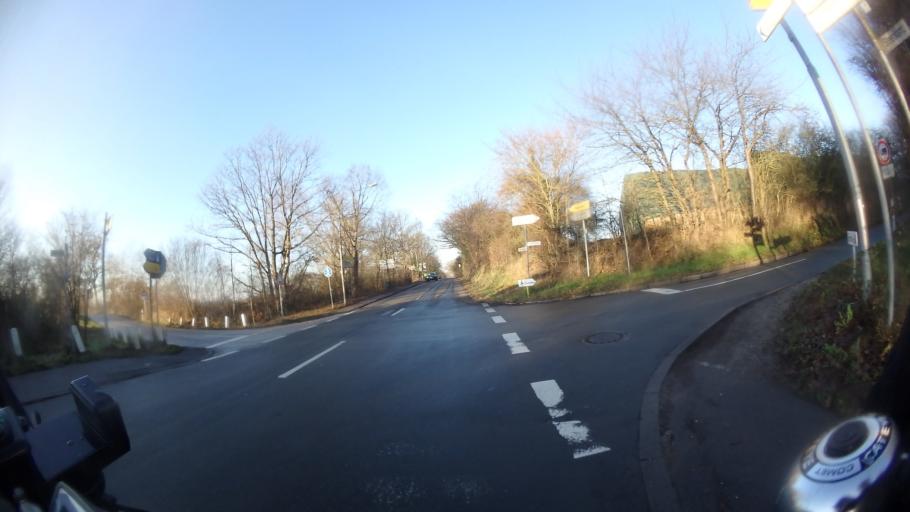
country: DE
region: Schleswig-Holstein
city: Travemuende
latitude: 53.9739
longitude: 10.8675
